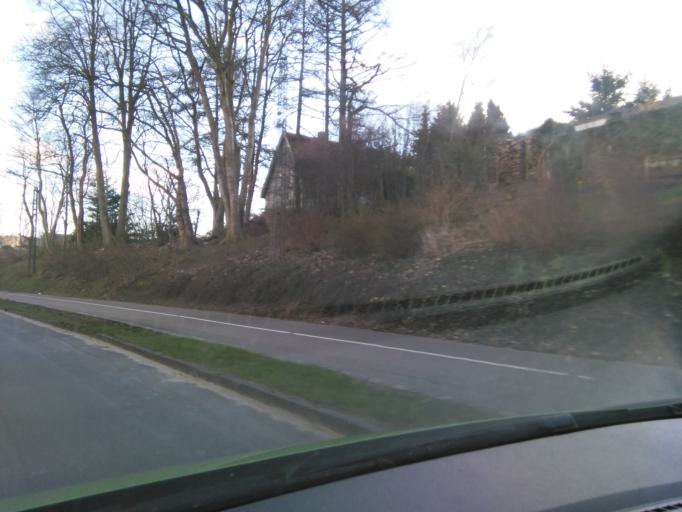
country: DK
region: Central Jutland
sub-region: Silkeborg Kommune
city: Silkeborg
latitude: 56.1783
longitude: 9.5196
